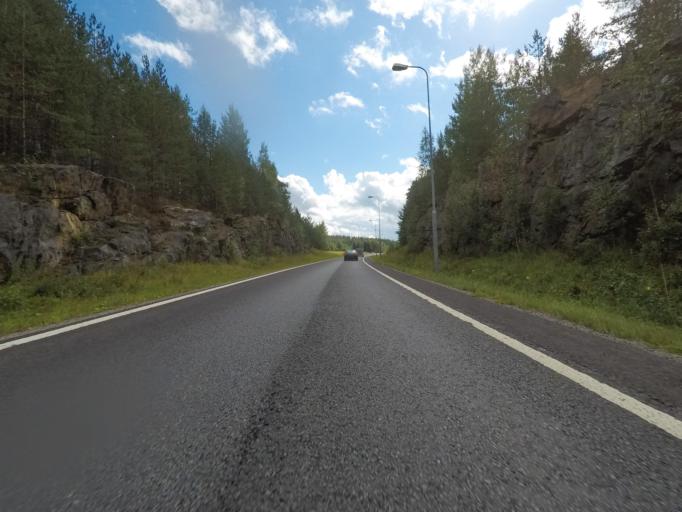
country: FI
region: Paijanne Tavastia
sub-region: Lahti
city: Heinola
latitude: 61.2909
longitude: 26.0742
